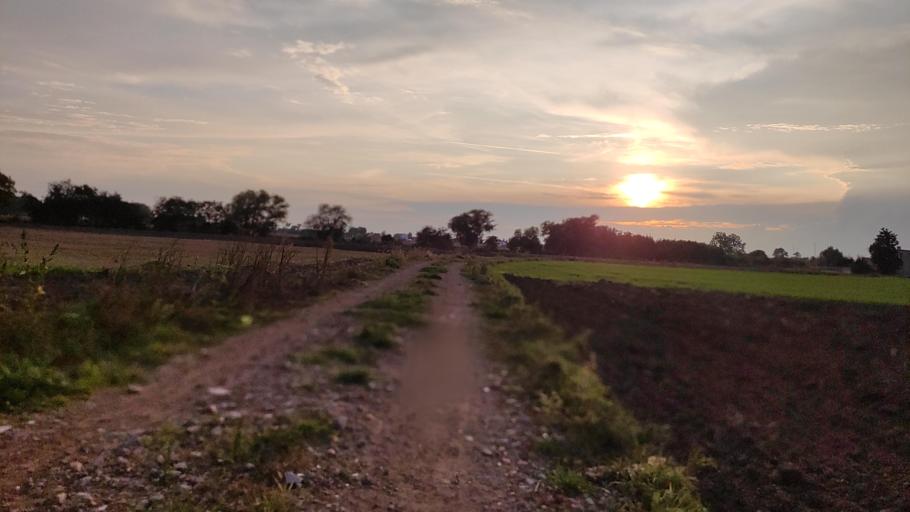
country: PL
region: Greater Poland Voivodeship
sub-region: Powiat poznanski
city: Kleszczewo
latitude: 52.3885
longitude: 17.1740
